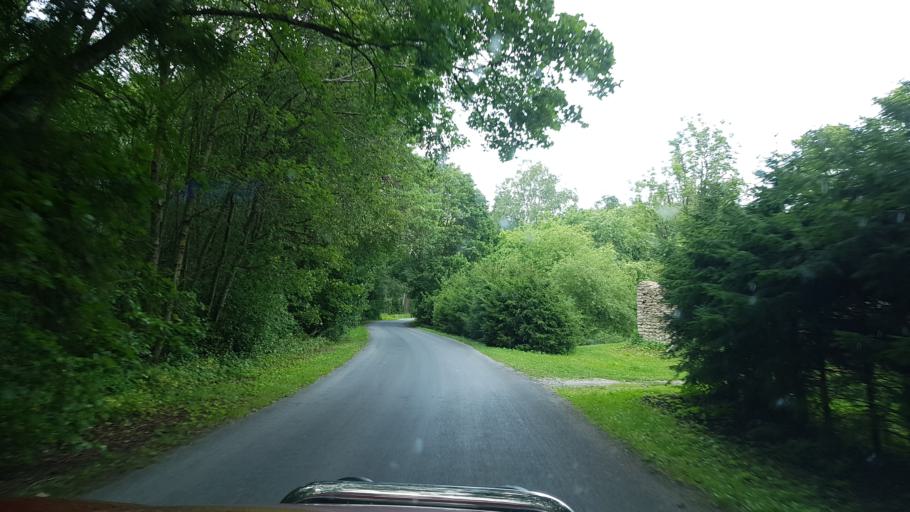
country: EE
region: Laeaene
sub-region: Ridala Parish
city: Uuemoisa
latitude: 59.0036
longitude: 23.7220
